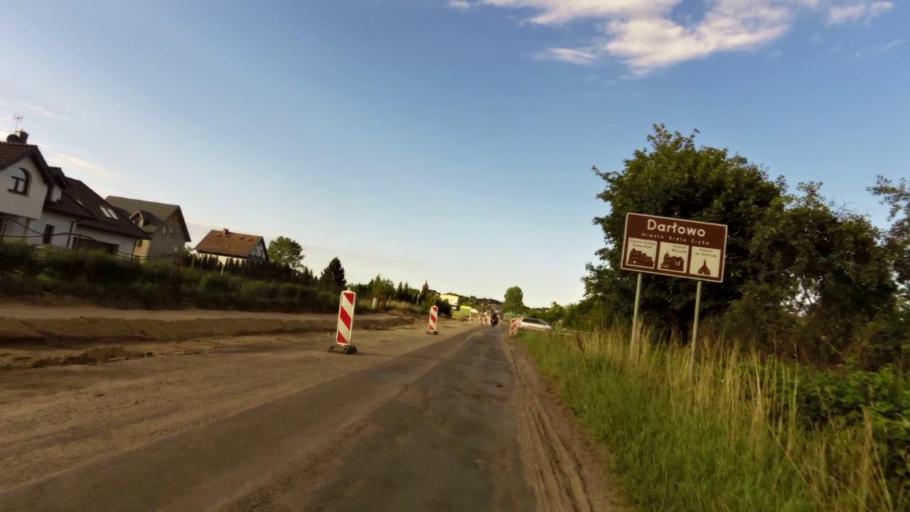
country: PL
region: West Pomeranian Voivodeship
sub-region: Powiat slawienski
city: Darlowo
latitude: 54.4119
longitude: 16.3968
